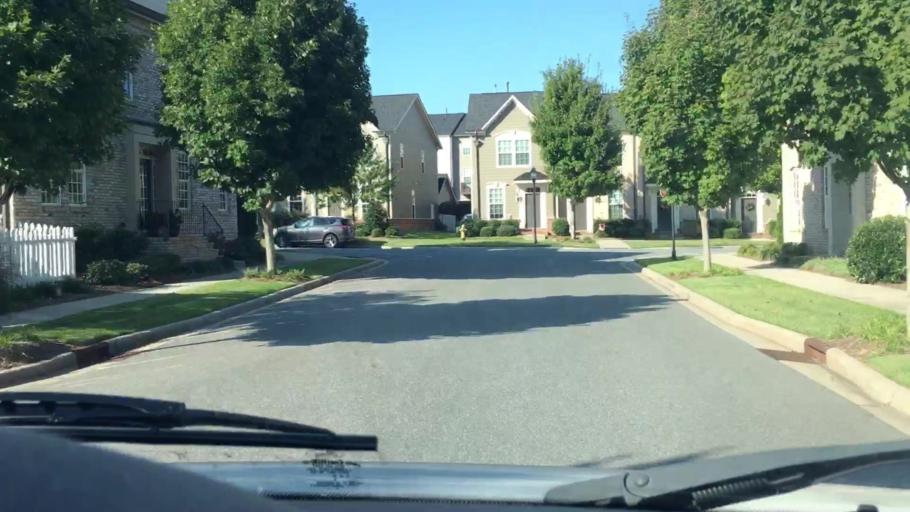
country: US
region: North Carolina
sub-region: Mecklenburg County
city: Cornelius
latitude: 35.4832
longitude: -80.8526
